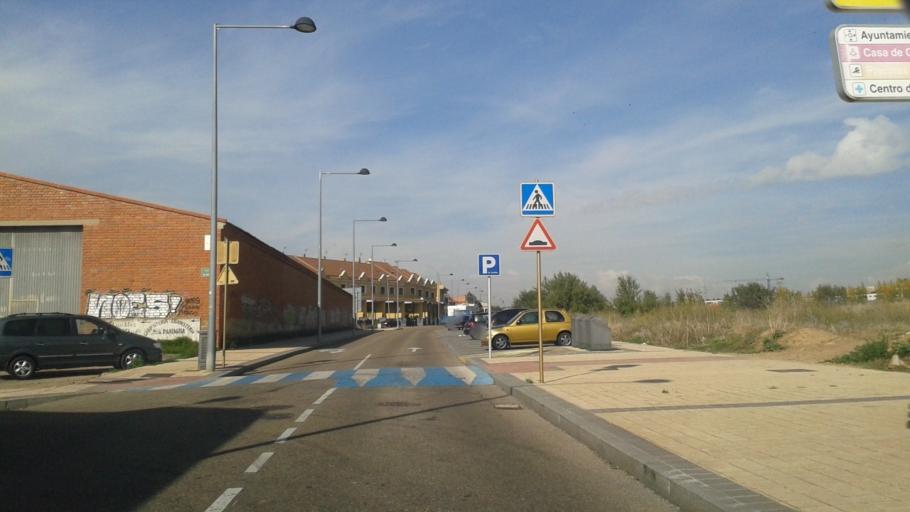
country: ES
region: Castille and Leon
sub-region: Provincia de Valladolid
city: Arroyo
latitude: 41.6285
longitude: -4.7704
